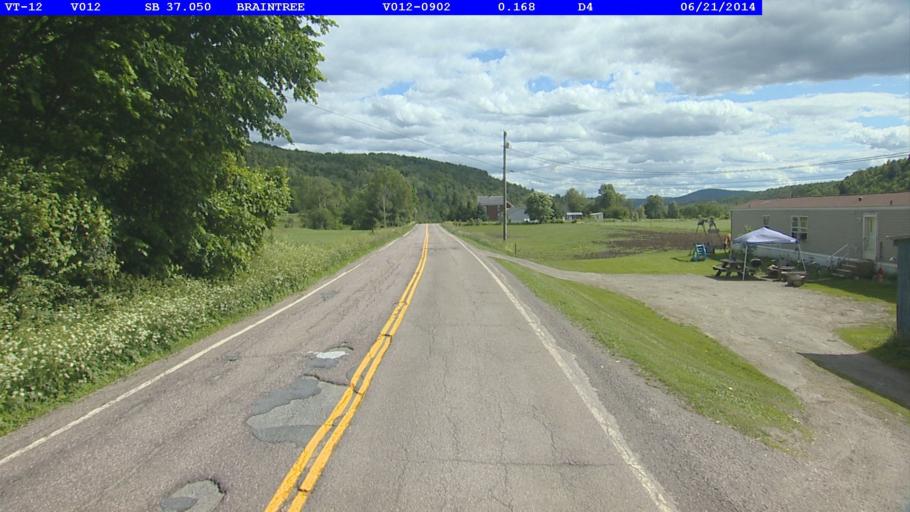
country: US
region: Vermont
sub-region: Orange County
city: Randolph
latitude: 43.9869
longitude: -72.6494
